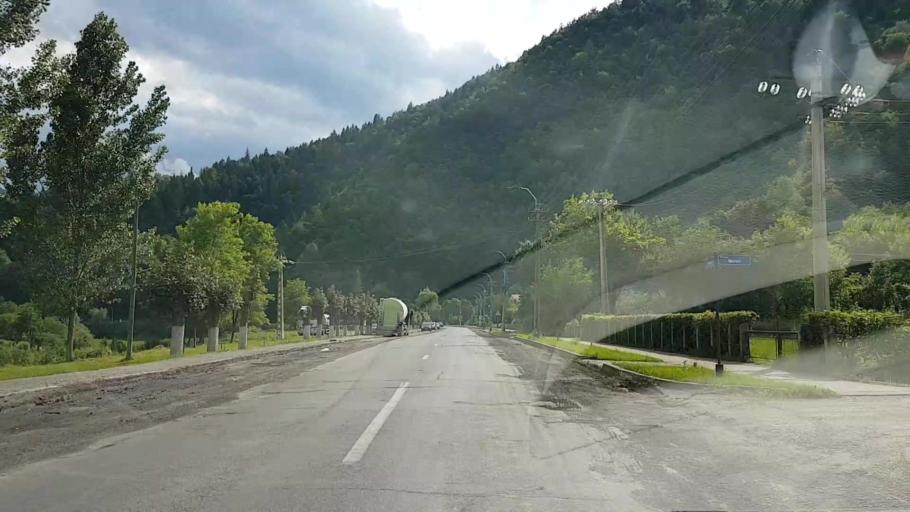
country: RO
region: Neamt
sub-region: Comuna Bicaz
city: Dodeni
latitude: 46.9207
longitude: 26.0877
